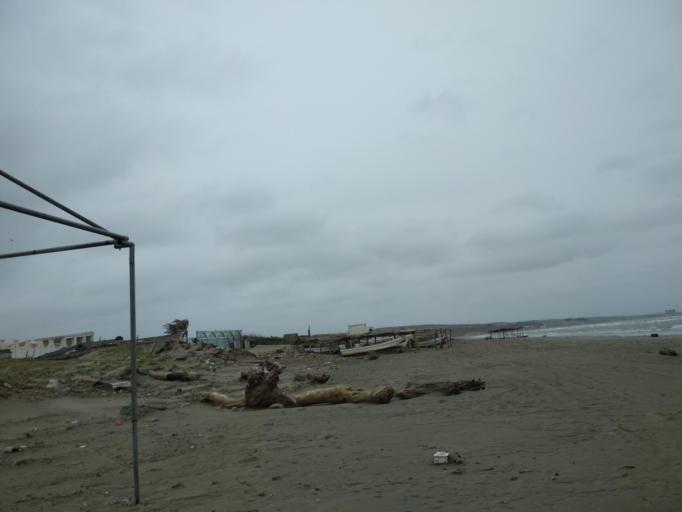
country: MX
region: Veracruz
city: Anton Lizardo
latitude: 19.0612
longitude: -95.9976
